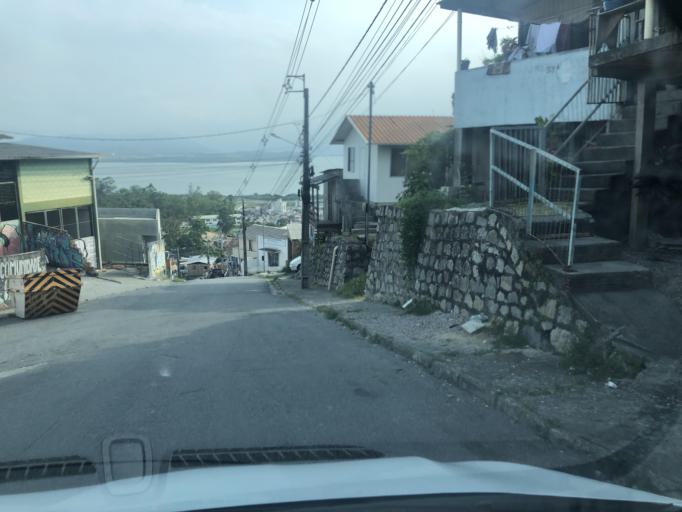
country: BR
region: Santa Catarina
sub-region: Florianopolis
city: Carvoeira
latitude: -27.5966
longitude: -48.5324
